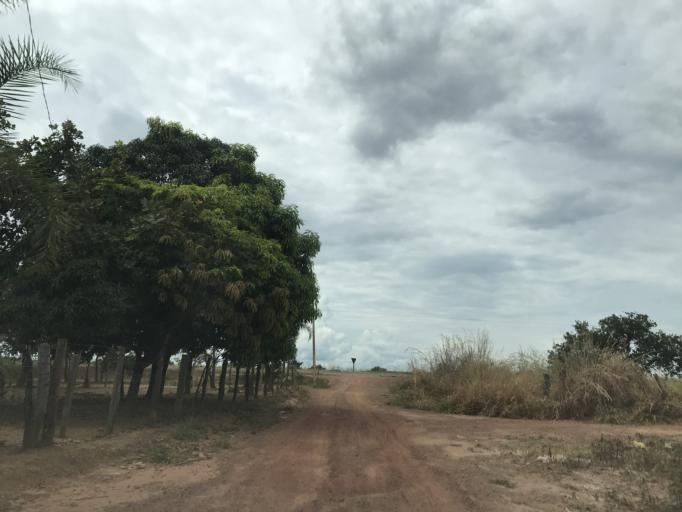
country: BR
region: Goias
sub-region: Padre Bernardo
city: Padre Bernardo
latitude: -15.3573
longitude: -48.2294
